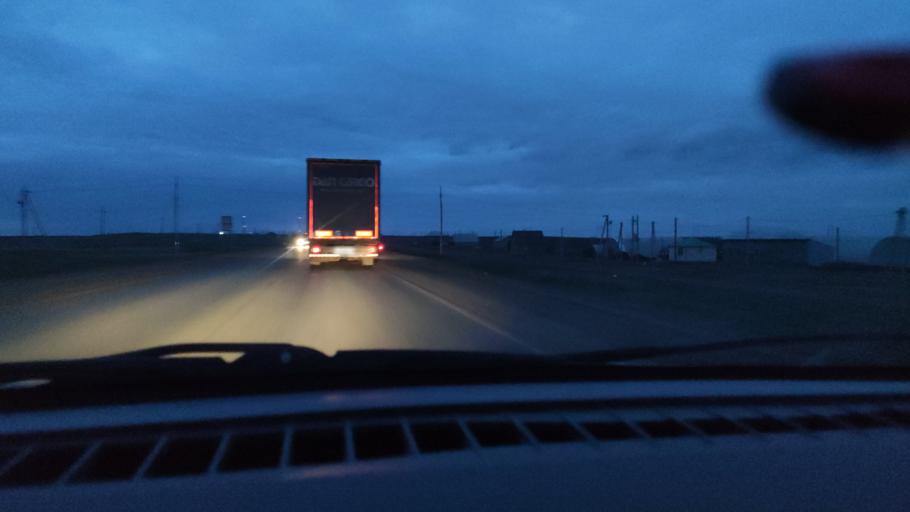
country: RU
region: Orenburg
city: Tatarskaya Kargala
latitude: 51.9591
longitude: 55.1839
